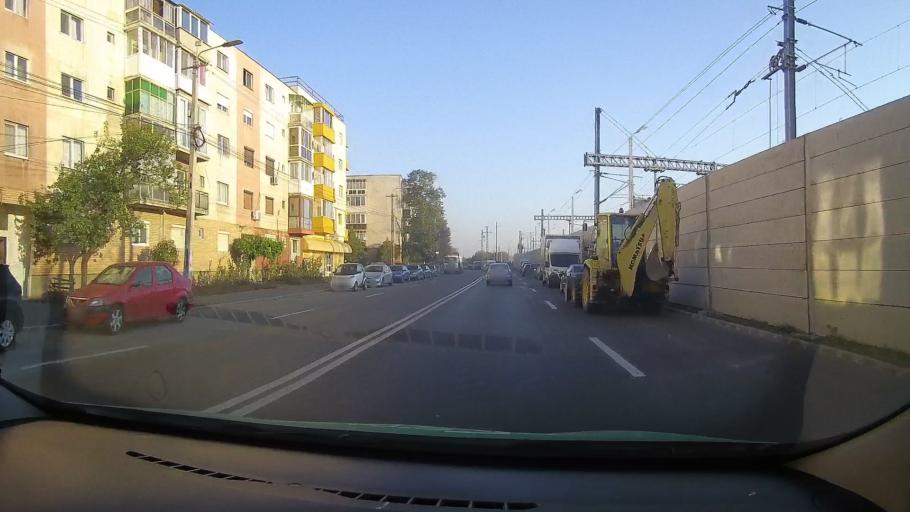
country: RO
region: Arad
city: Arad
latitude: 46.1978
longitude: 21.3204
